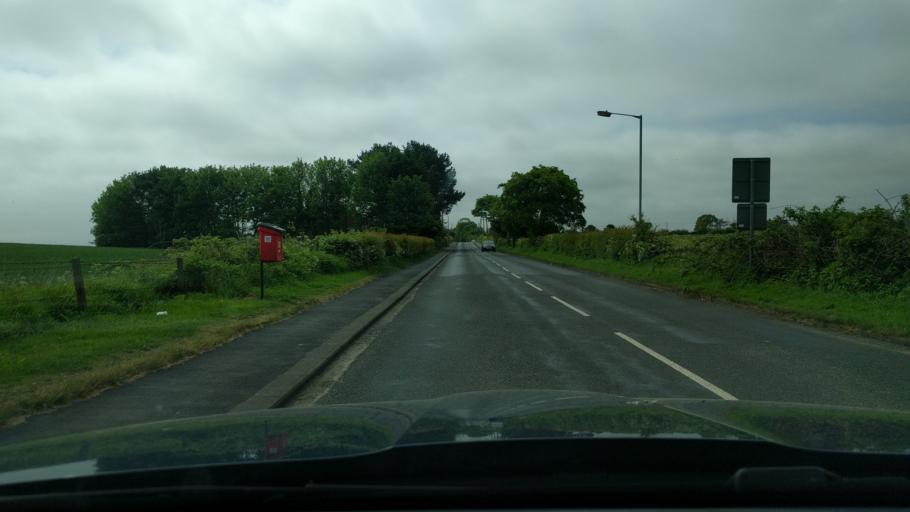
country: GB
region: England
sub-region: Northumberland
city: Acklington
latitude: 55.3006
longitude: -1.6123
